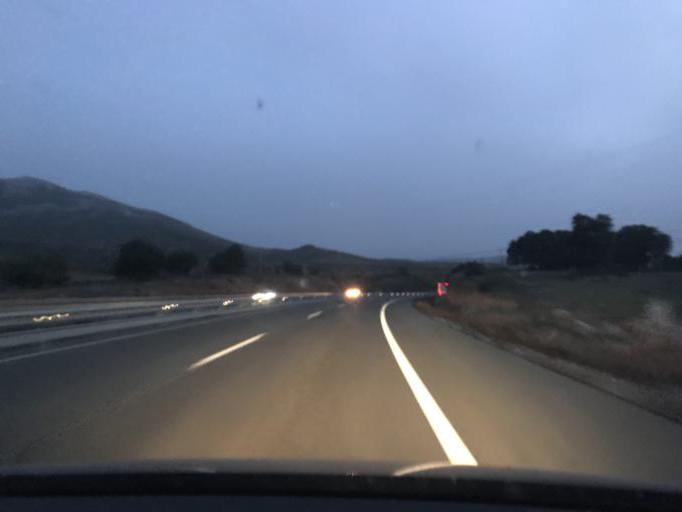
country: ES
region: Andalusia
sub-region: Provincia de Granada
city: Gor
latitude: 37.4101
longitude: -2.9189
